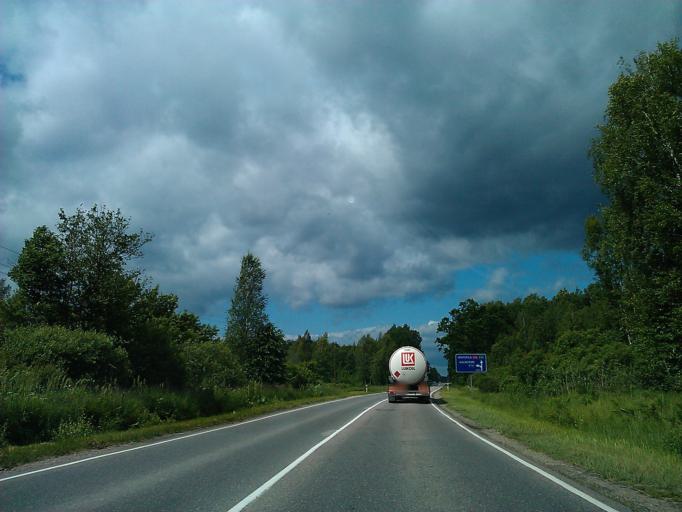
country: LV
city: Tireli
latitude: 56.9263
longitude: 23.5379
